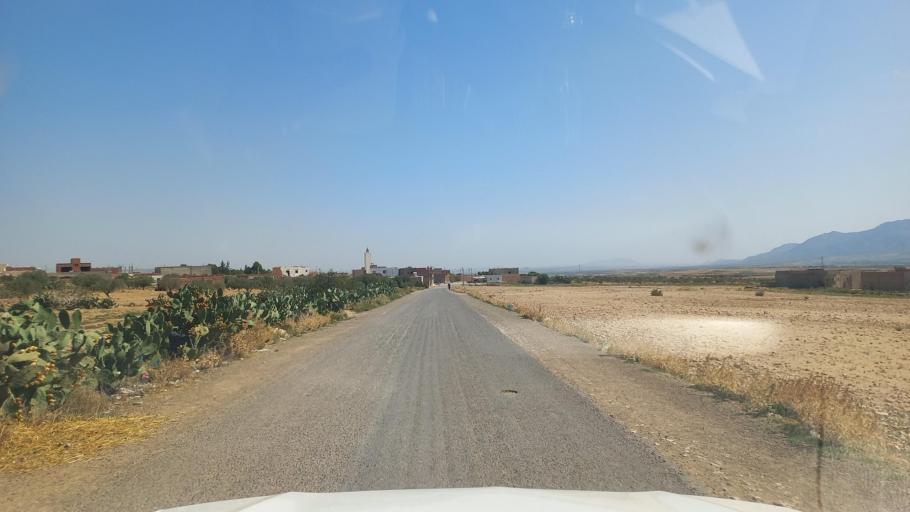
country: TN
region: Al Qasrayn
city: Sbiba
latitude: 35.4432
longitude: 9.0750
